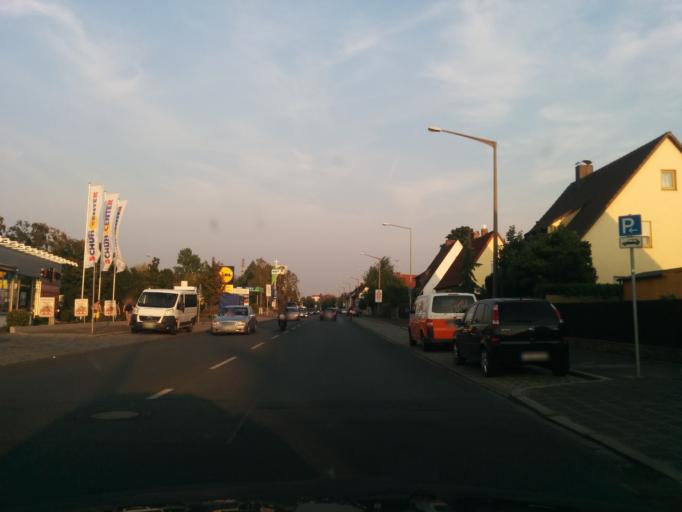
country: DE
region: Bavaria
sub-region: Regierungsbezirk Mittelfranken
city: Wetzendorf
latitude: 49.4708
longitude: 11.0245
